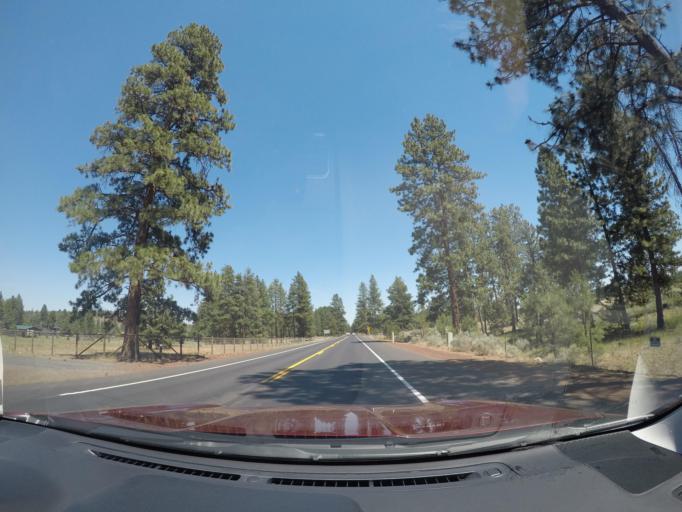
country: US
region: Oregon
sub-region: Deschutes County
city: Sisters
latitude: 44.2878
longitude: -121.5337
